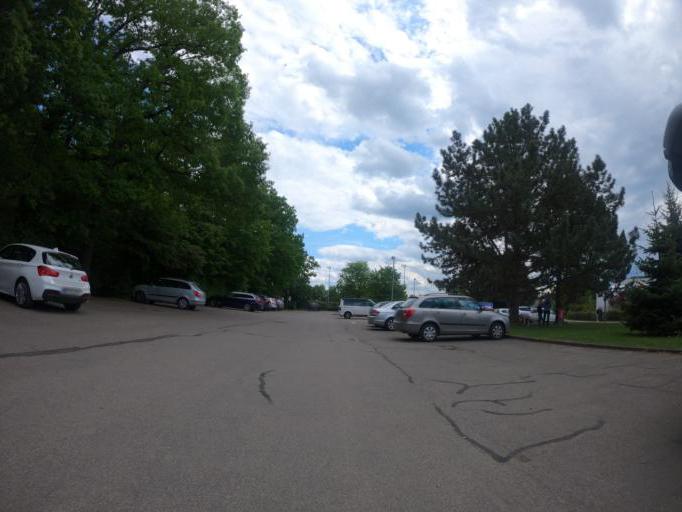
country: DE
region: Baden-Wuerttemberg
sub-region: Regierungsbezirk Stuttgart
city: Holzgerlingen
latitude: 48.6481
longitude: 9.0166
